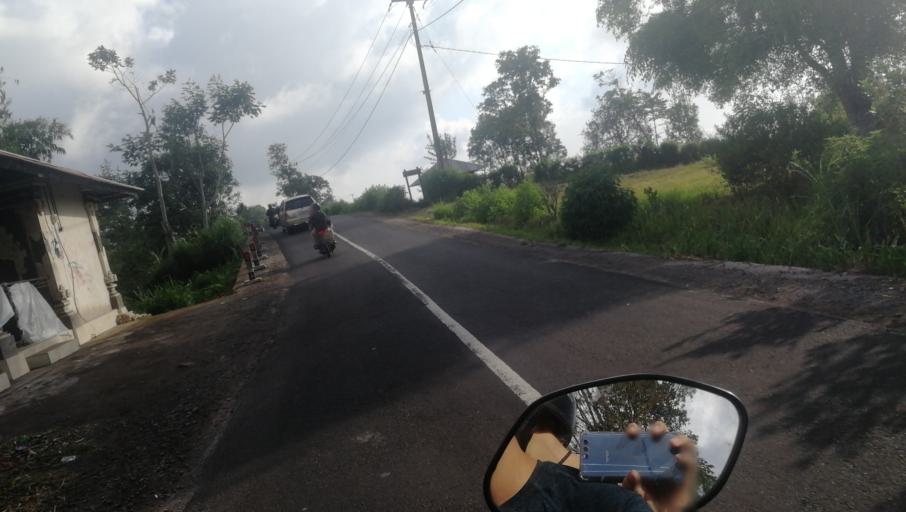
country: ID
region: Bali
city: Munduk
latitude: -8.2570
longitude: 115.0901
